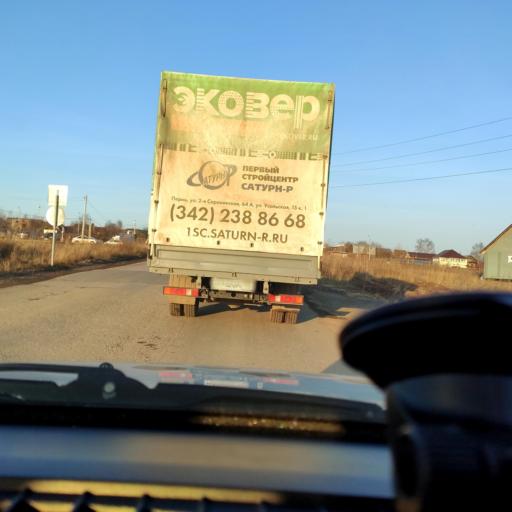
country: RU
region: Perm
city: Ferma
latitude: 57.9550
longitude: 56.3700
